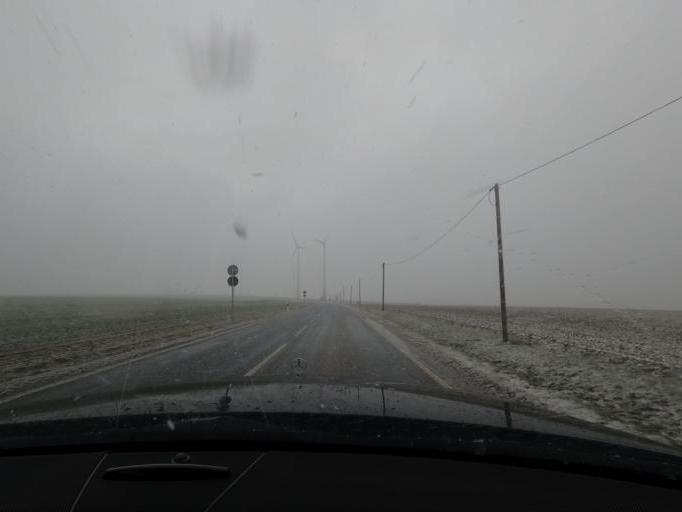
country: DE
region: Thuringia
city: Buttstedt
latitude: 51.2282
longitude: 10.2995
